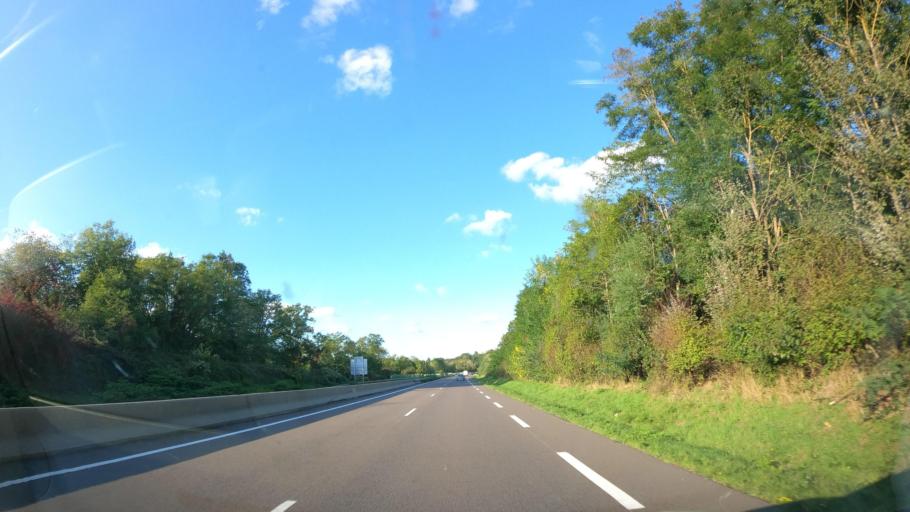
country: FR
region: Bourgogne
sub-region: Departement de Saone-et-Loire
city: Montceau-les-Mines
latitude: 46.6762
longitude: 4.3456
